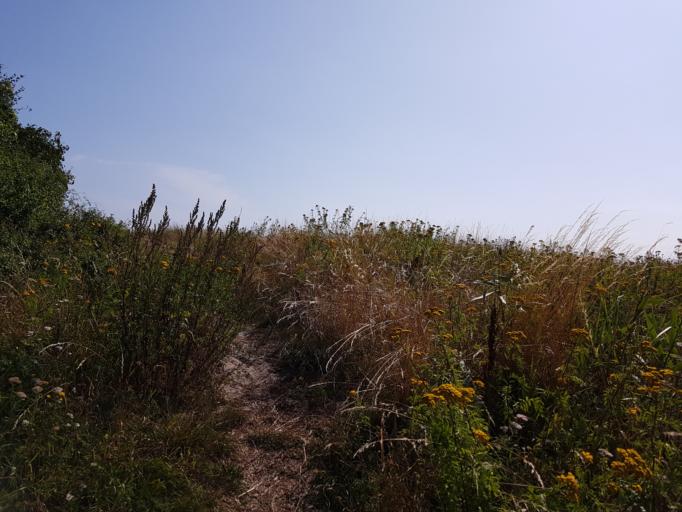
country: DK
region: Zealand
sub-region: Guldborgsund Kommune
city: Nykobing Falster
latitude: 54.5750
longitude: 11.9214
